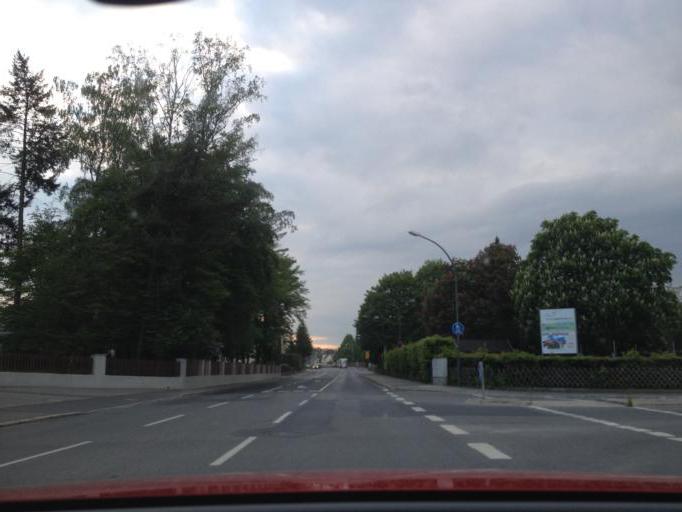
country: DE
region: Bavaria
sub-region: Upper Palatinate
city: Hirschau
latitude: 49.5435
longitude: 11.9526
